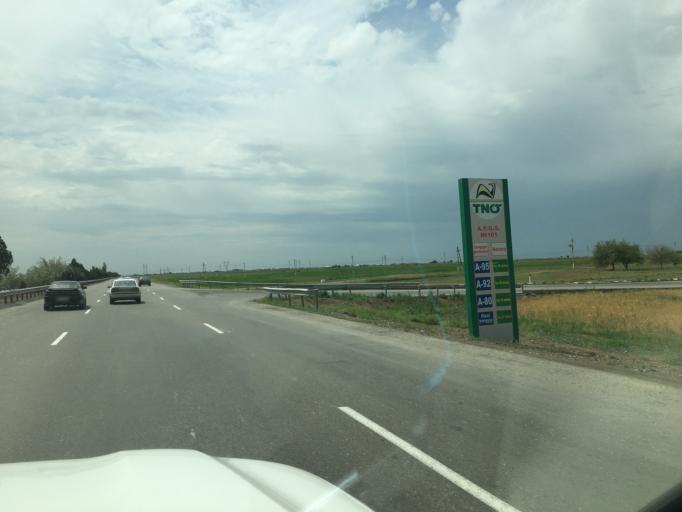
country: TM
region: Mary
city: Bayramaly
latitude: 37.6219
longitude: 62.1011
